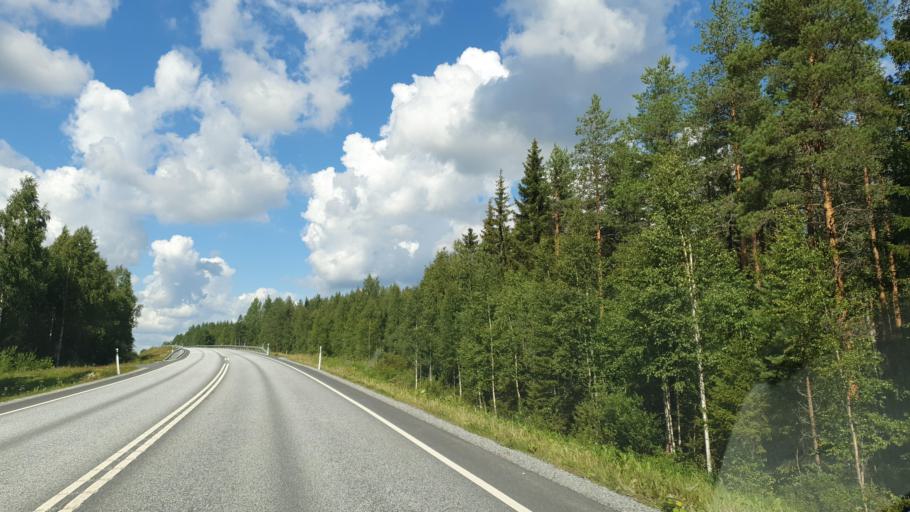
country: FI
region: Northern Savo
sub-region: Ylae-Savo
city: Sonkajaervi
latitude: 63.8866
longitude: 27.4360
